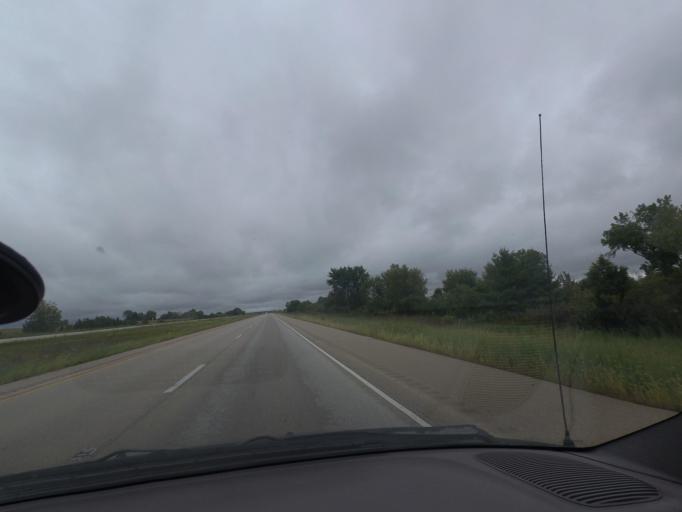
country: US
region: Illinois
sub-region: Piatt County
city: Cerro Gordo
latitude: 39.9467
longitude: -88.8295
